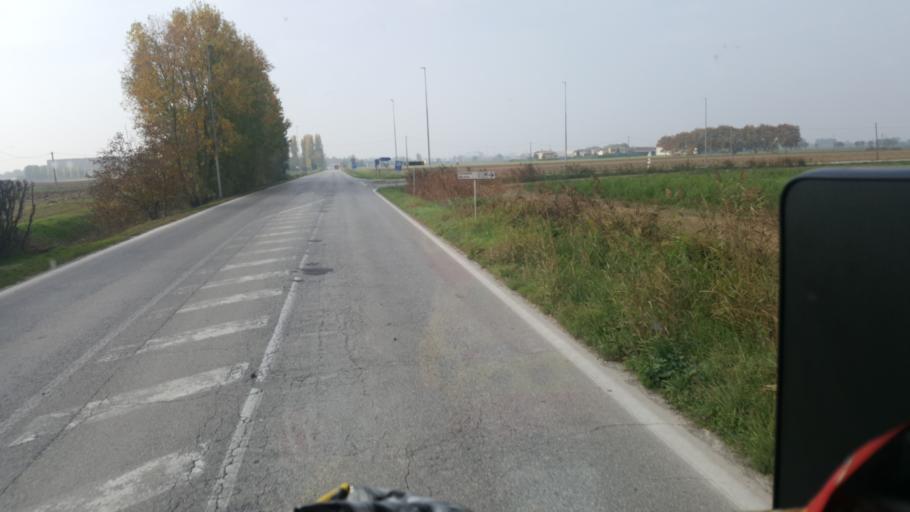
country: IT
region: Lombardy
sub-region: Provincia di Mantova
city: Rodigo
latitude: 45.2128
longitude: 10.6026
